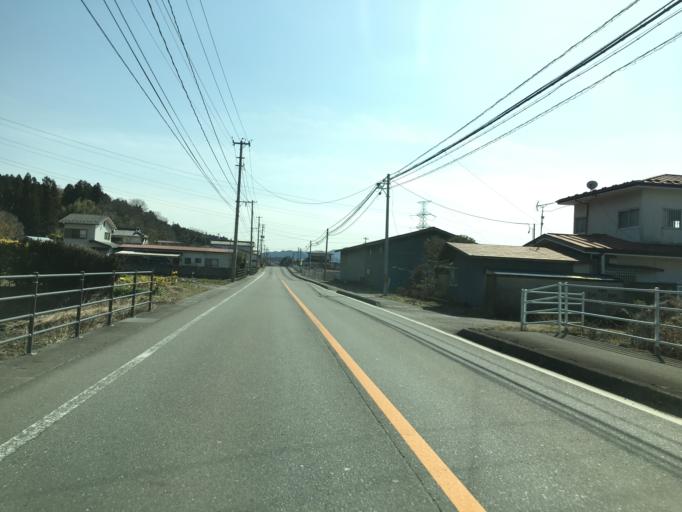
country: JP
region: Ibaraki
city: Daigo
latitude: 36.9037
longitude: 140.4182
